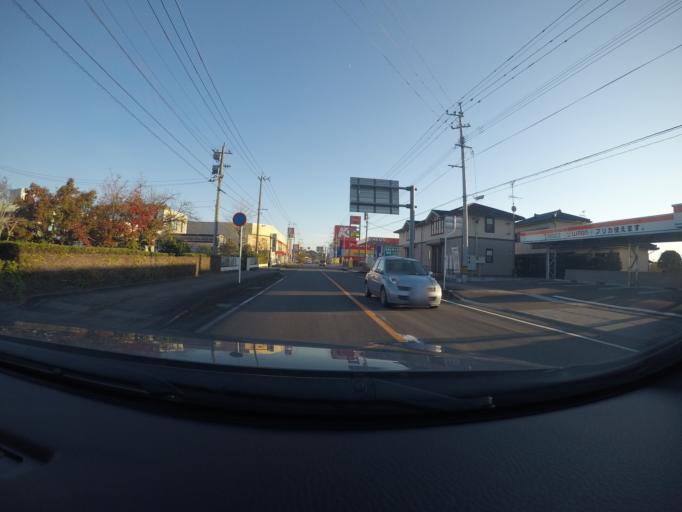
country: JP
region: Kagoshima
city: Okuchi-shinohara
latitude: 32.0589
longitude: 130.6058
